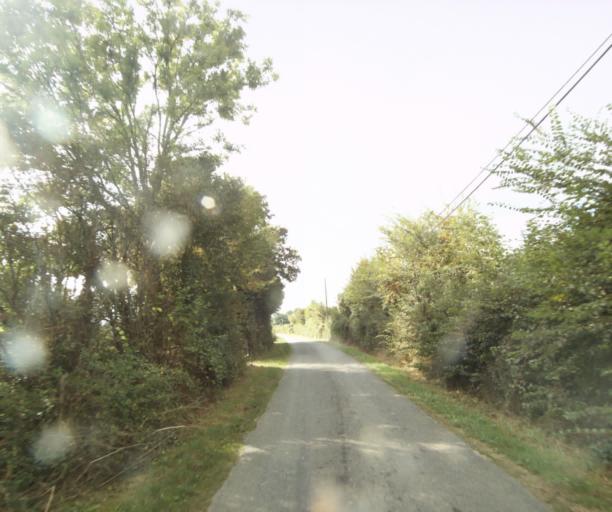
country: FR
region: Bourgogne
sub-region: Departement de Saone-et-Loire
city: Palinges
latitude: 46.5285
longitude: 4.2780
